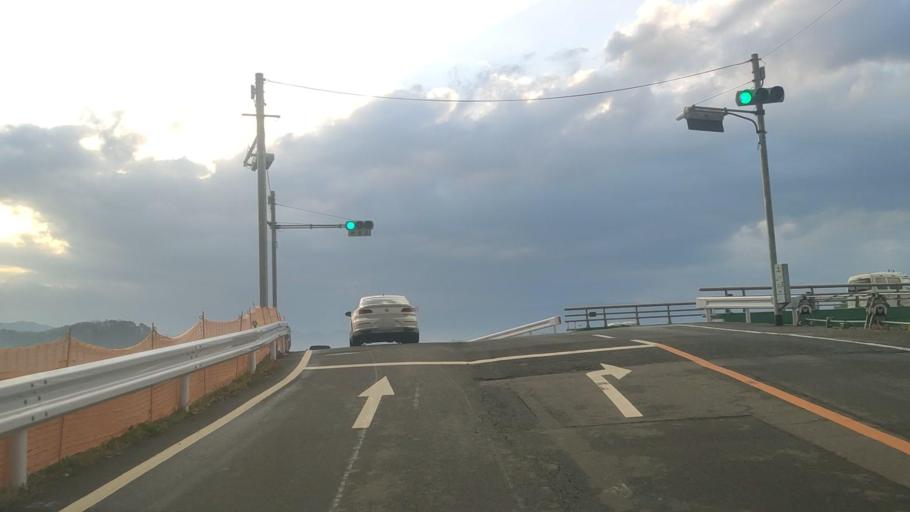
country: JP
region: Kumamoto
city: Uto
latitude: 32.7023
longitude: 130.7790
